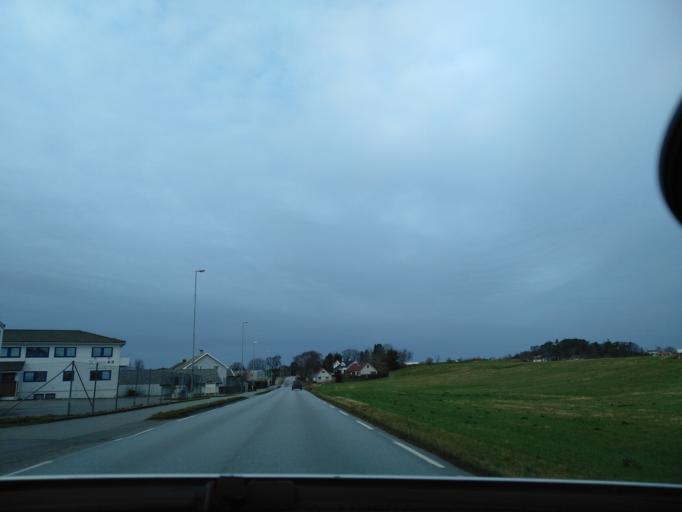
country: NO
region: Rogaland
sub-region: Randaberg
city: Randaberg
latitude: 58.9962
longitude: 5.6319
